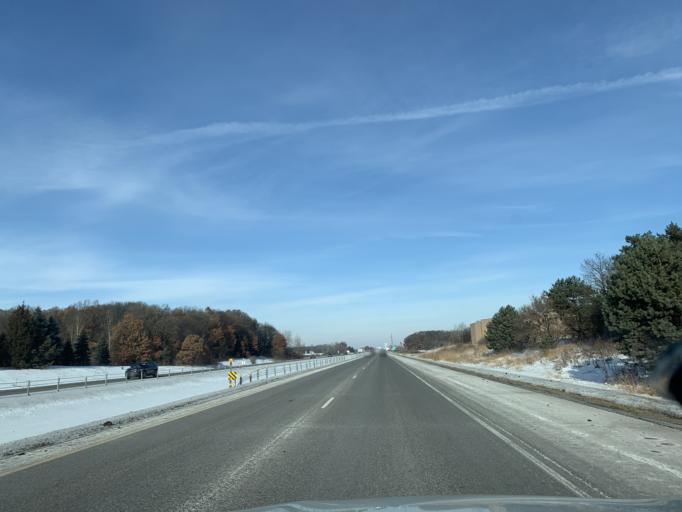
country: US
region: Minnesota
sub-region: Chisago County
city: Wyoming
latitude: 45.3152
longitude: -93.0033
